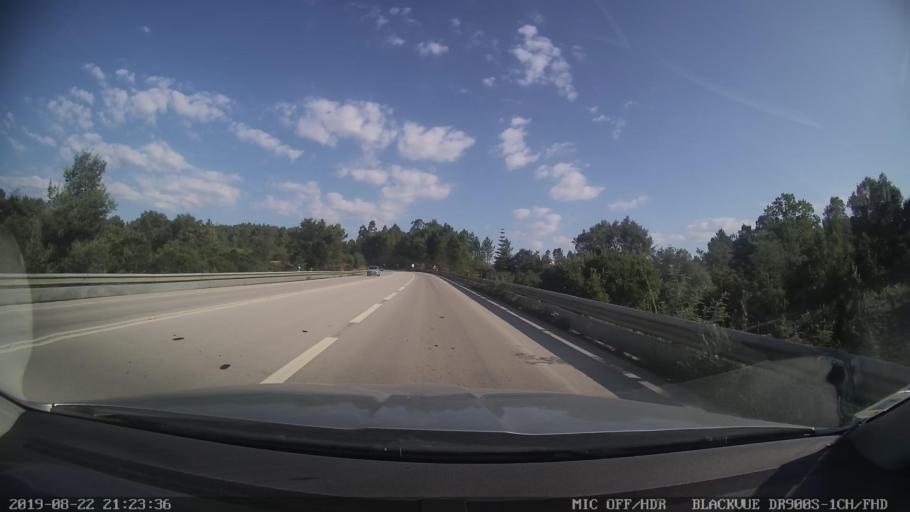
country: PT
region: Castelo Branco
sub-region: Serta
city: Serta
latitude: 39.8329
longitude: -8.1104
